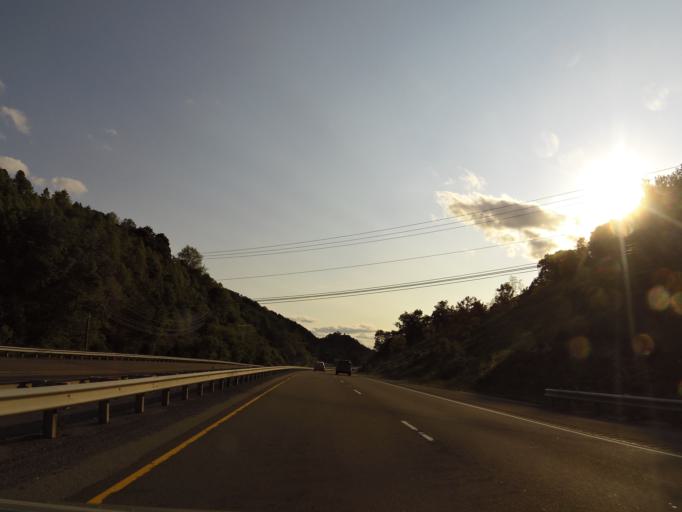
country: US
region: Virginia
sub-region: Russell County
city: Lebanon
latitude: 36.9133
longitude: -82.0145
